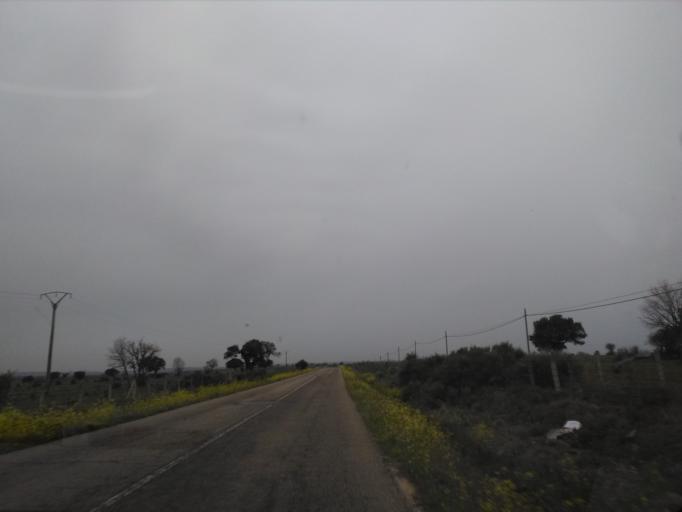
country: ES
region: Castille and Leon
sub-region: Provincia de Salamanca
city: Moronta
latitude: 40.9883
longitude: -6.4558
